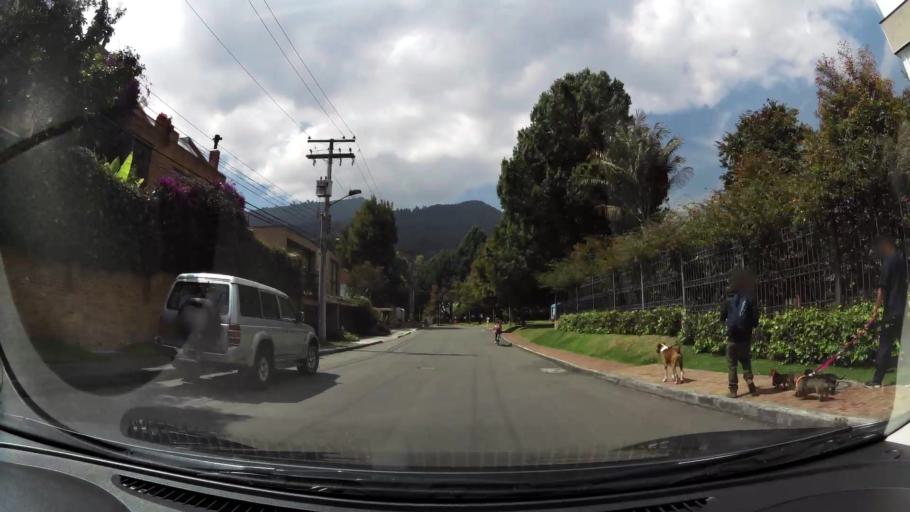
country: CO
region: Bogota D.C.
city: Barrio San Luis
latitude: 4.6866
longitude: -74.0333
